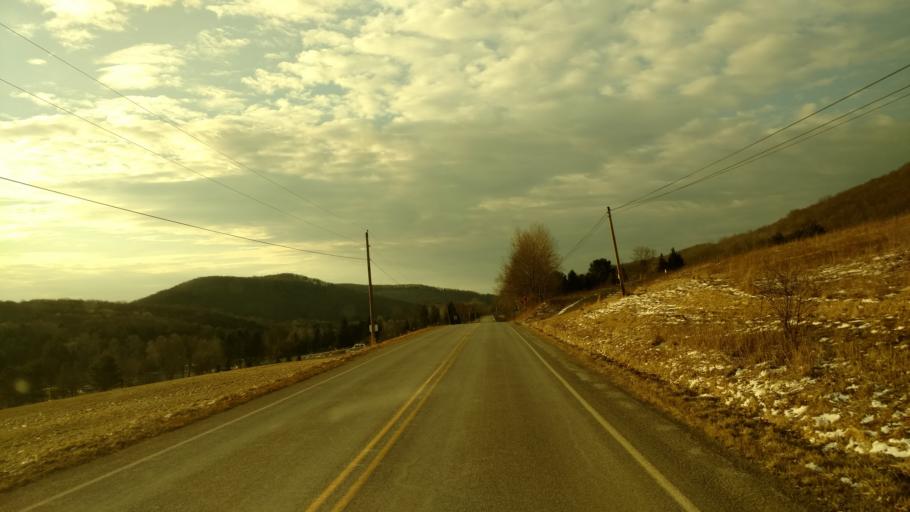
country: US
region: New York
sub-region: Allegany County
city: Wellsville
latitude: 41.9764
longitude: -77.8620
